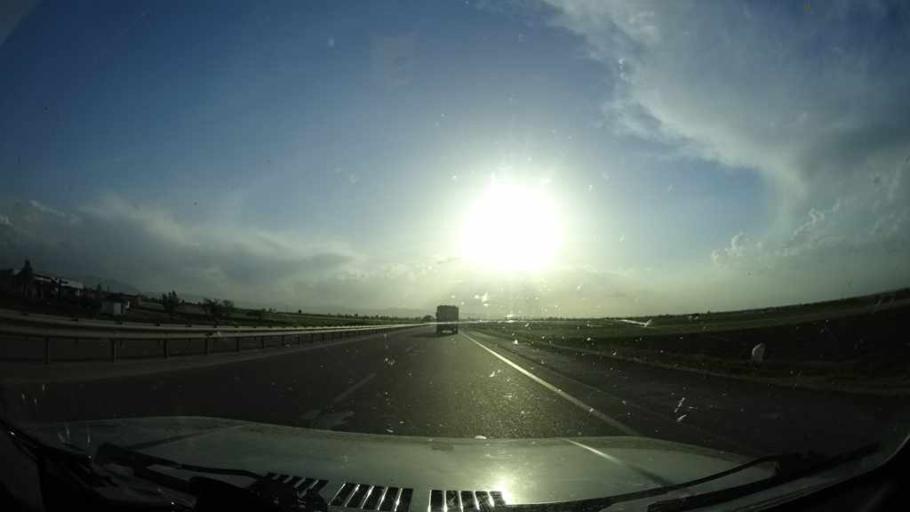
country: AZ
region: Samux
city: Samux
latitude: 40.6896
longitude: 46.5341
